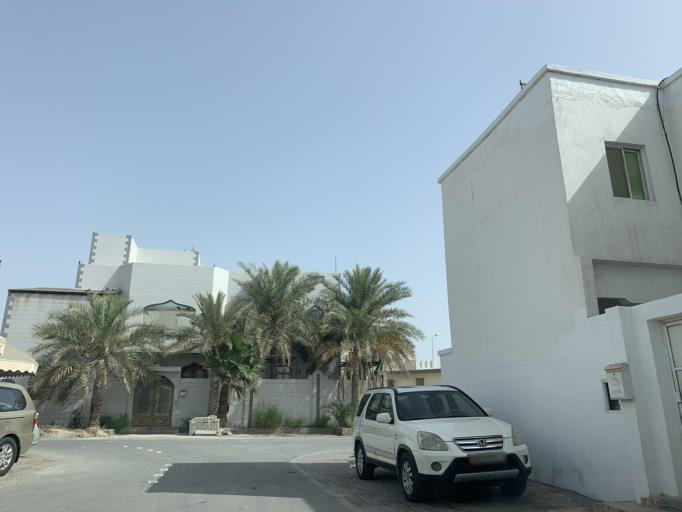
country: BH
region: Northern
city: Sitrah
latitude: 26.1313
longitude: 50.5974
